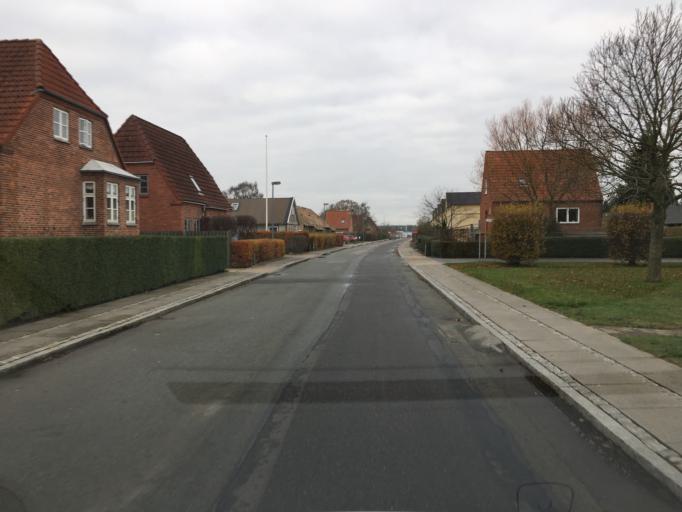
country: DK
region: South Denmark
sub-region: Tonder Kommune
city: Tonder
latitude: 54.9448
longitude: 8.8683
